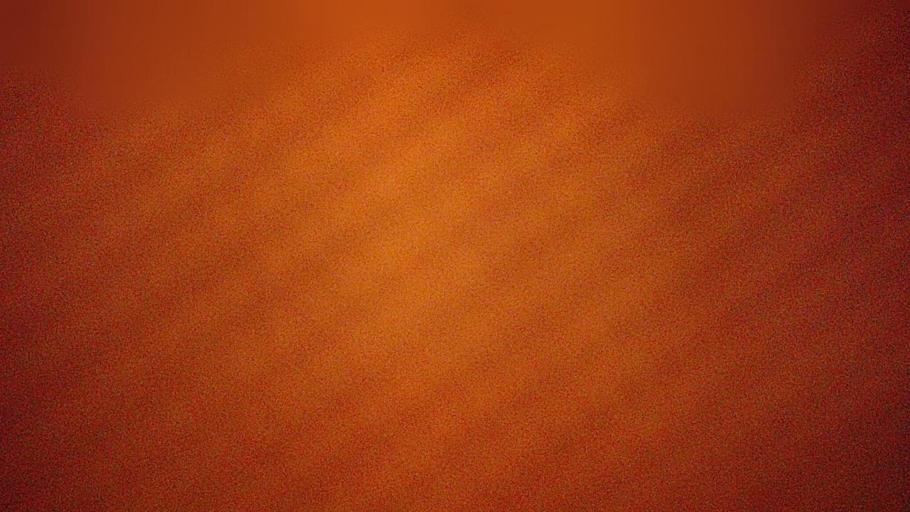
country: BO
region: La Paz
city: La Paz
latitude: -16.5366
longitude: -68.1352
